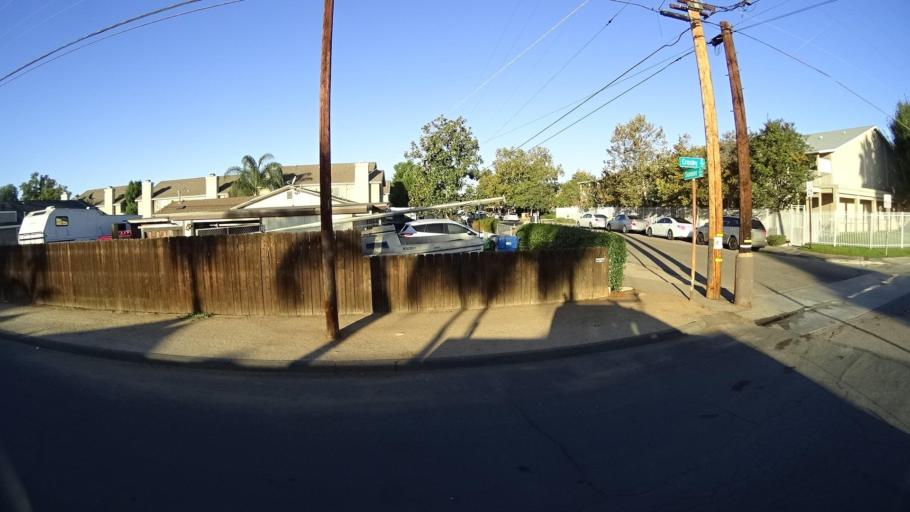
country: US
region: California
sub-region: San Diego County
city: Bostonia
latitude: 32.8096
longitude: -116.9379
